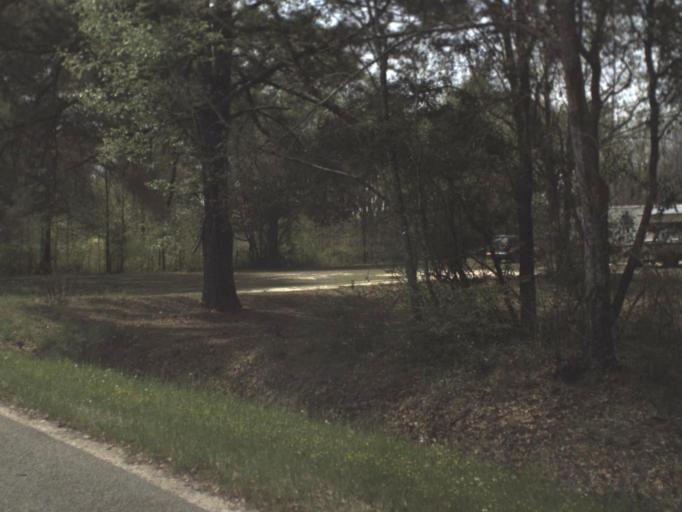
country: US
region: Florida
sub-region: Jackson County
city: Graceville
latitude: 30.9277
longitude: -85.5194
